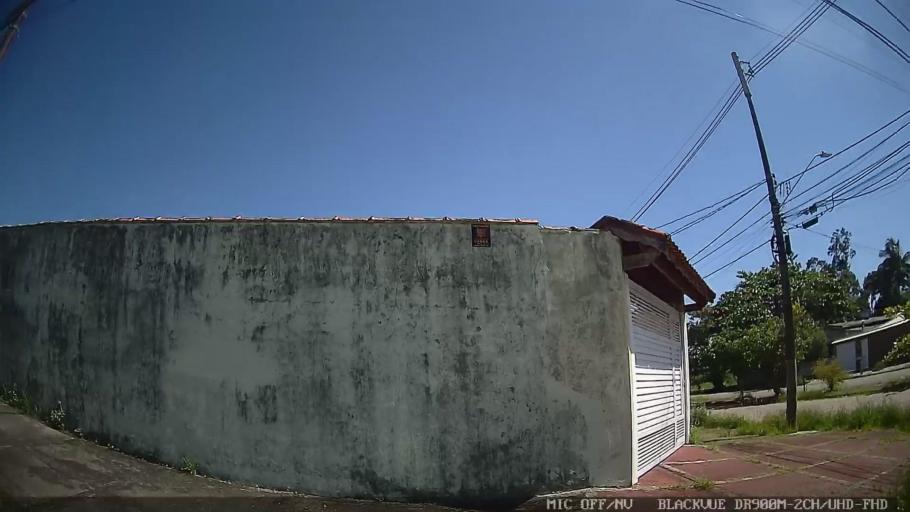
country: BR
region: Sao Paulo
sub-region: Peruibe
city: Peruibe
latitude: -24.3016
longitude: -46.9857
